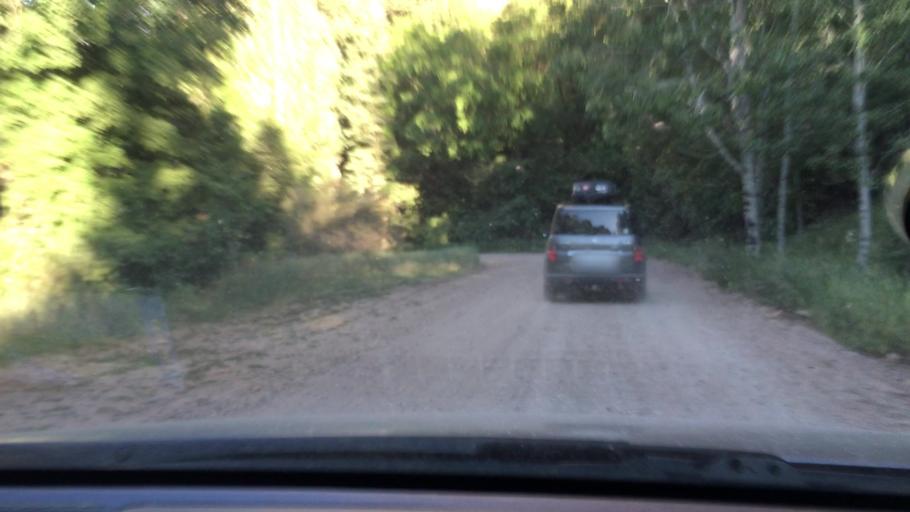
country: US
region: Utah
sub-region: Sanpete County
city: Fountain Green
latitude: 39.5550
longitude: -111.6794
